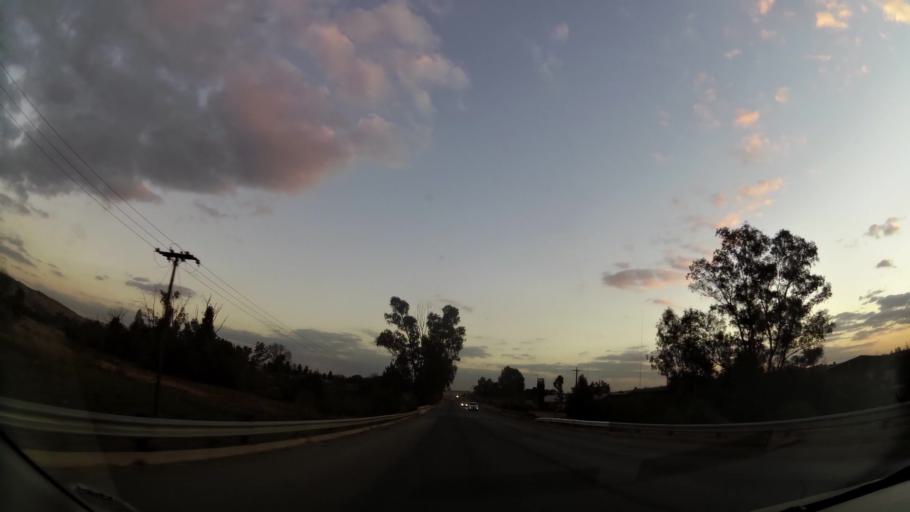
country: ZA
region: Gauteng
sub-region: West Rand District Municipality
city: Krugersdorp
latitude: -26.0392
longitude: 27.7217
